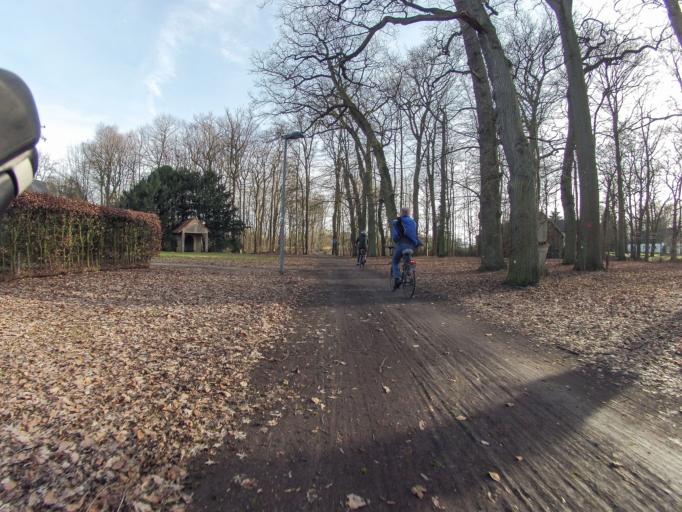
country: DE
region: North Rhine-Westphalia
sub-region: Regierungsbezirk Munster
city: Rheine
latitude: 52.2653
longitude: 7.4519
